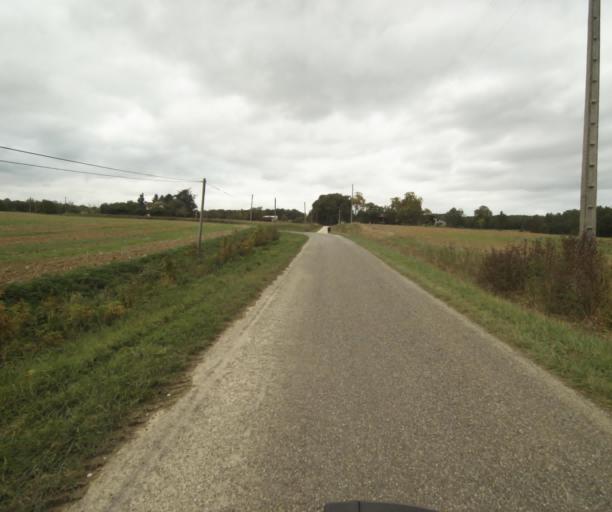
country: FR
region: Midi-Pyrenees
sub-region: Departement de la Haute-Garonne
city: Launac
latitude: 43.8415
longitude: 1.1072
